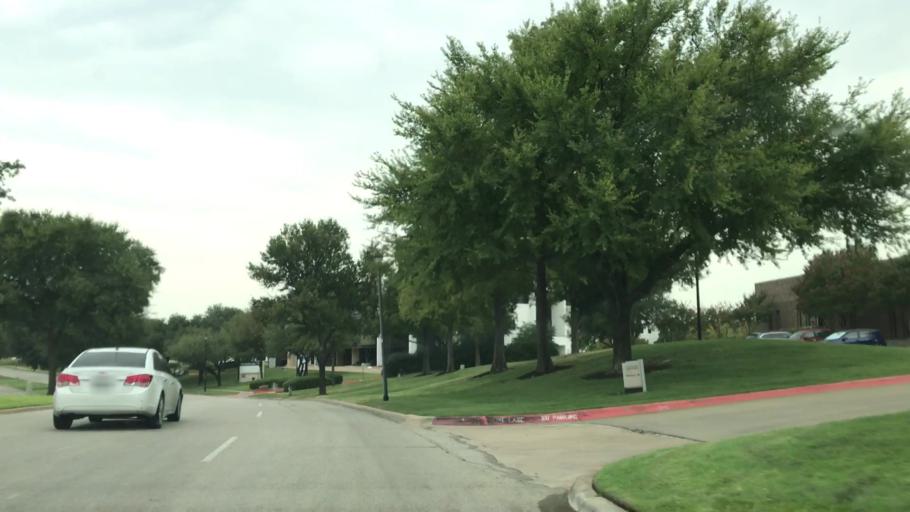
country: US
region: Texas
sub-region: Dallas County
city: Irving
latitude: 32.8817
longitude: -96.9751
